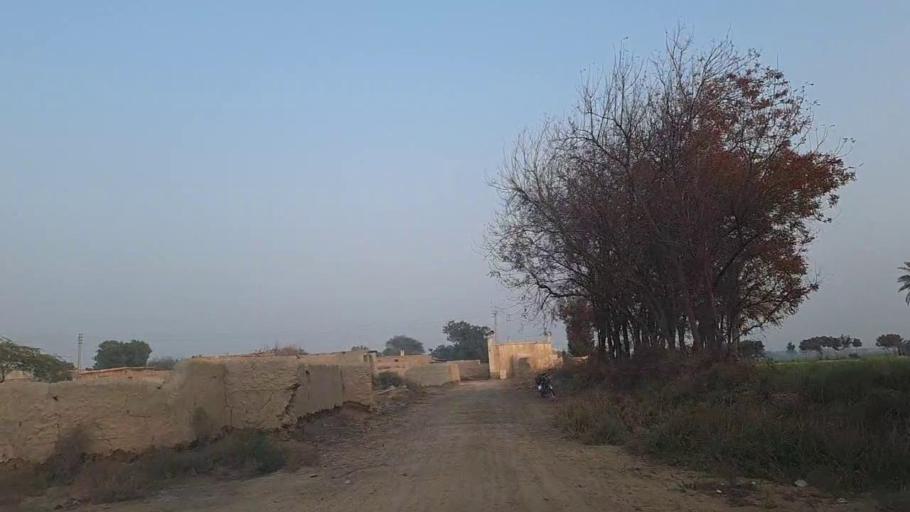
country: PK
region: Sindh
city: Nawabshah
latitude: 26.2811
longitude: 68.4659
